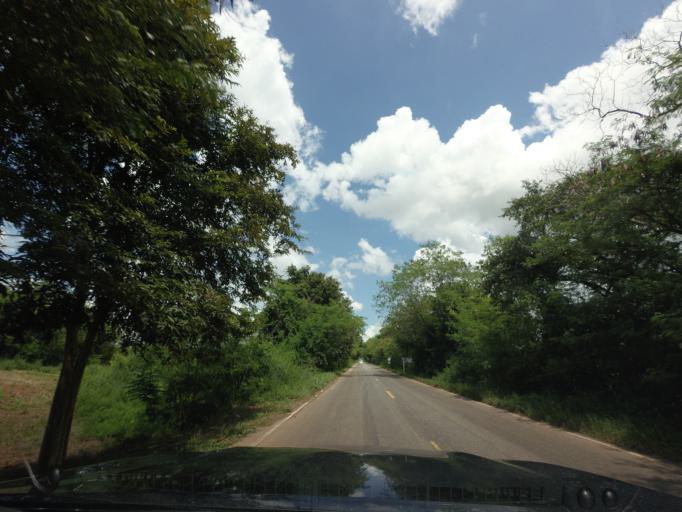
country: TH
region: Changwat Udon Thani
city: Ban Dung
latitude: 17.6716
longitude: 103.1714
